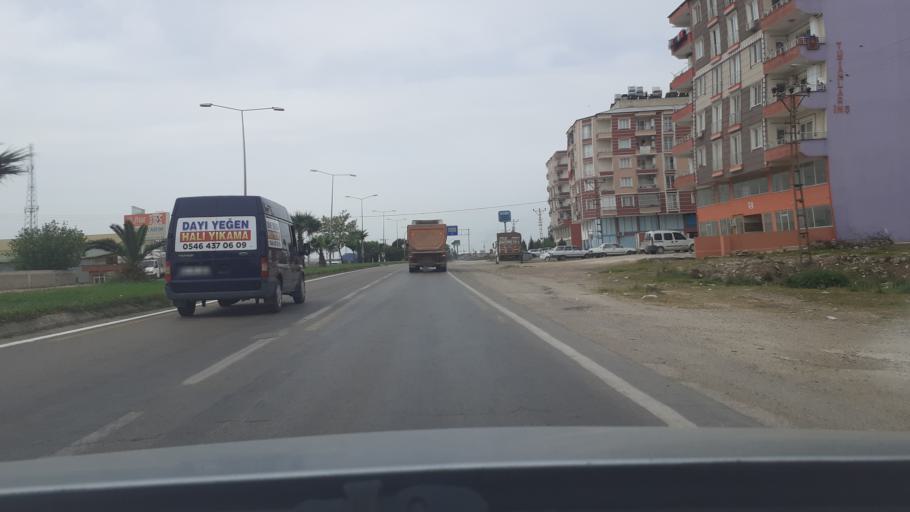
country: TR
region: Hatay
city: Kirikhan
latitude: 36.4904
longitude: 36.3691
